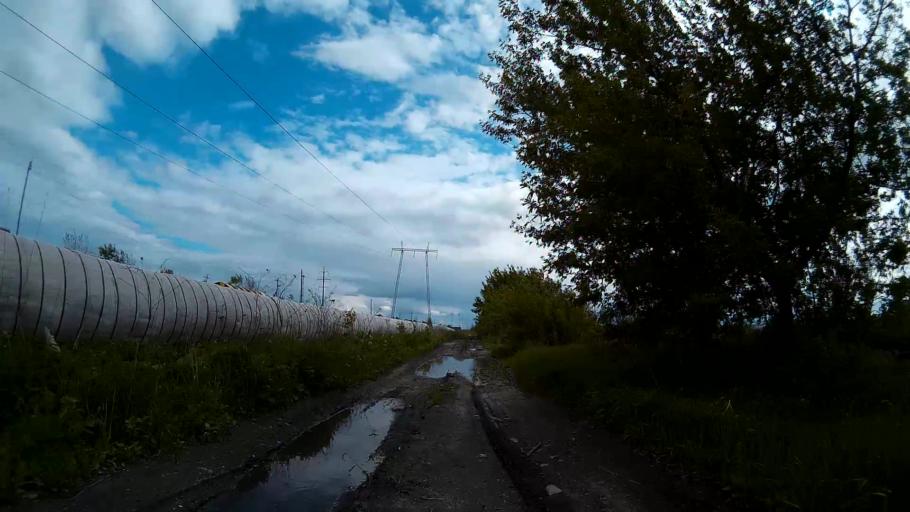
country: RU
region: Ulyanovsk
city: Novoul'yanovsk
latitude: 54.2361
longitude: 48.2953
